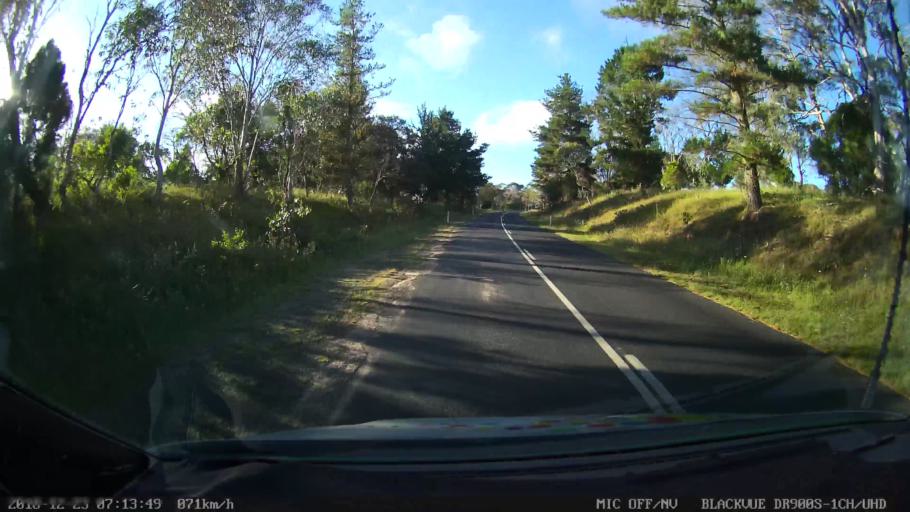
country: AU
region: New South Wales
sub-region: Bellingen
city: Dorrigo
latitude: -30.4284
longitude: 152.3247
